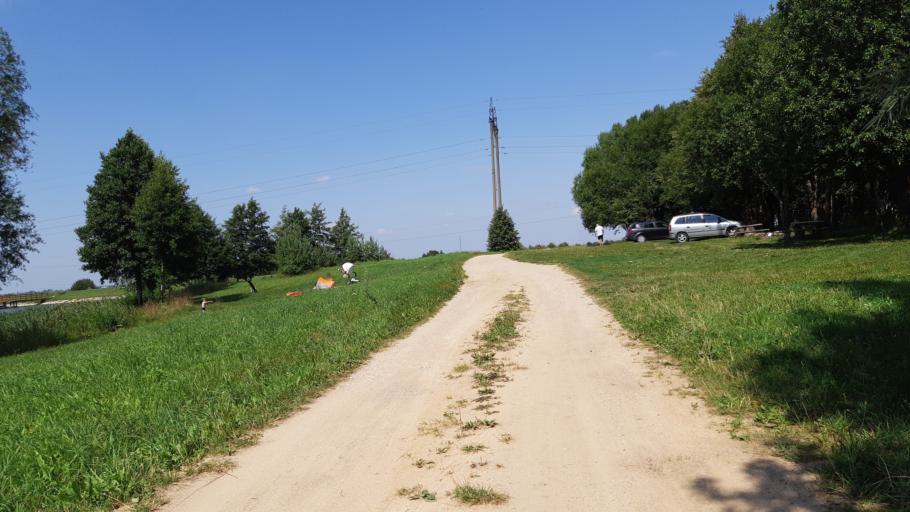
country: LT
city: Virbalis
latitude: 54.6178
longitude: 22.8035
